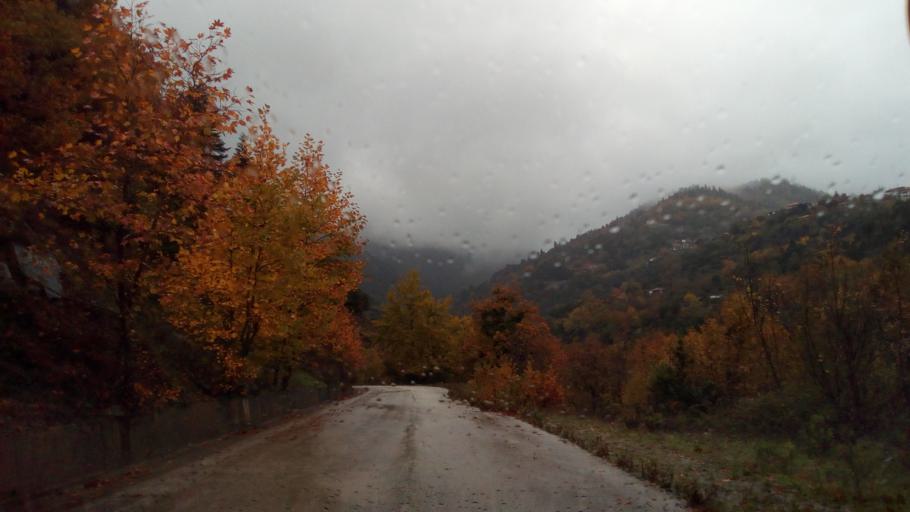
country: GR
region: West Greece
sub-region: Nomos Aitolias kai Akarnanias
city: Thermo
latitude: 38.6816
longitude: 21.8420
